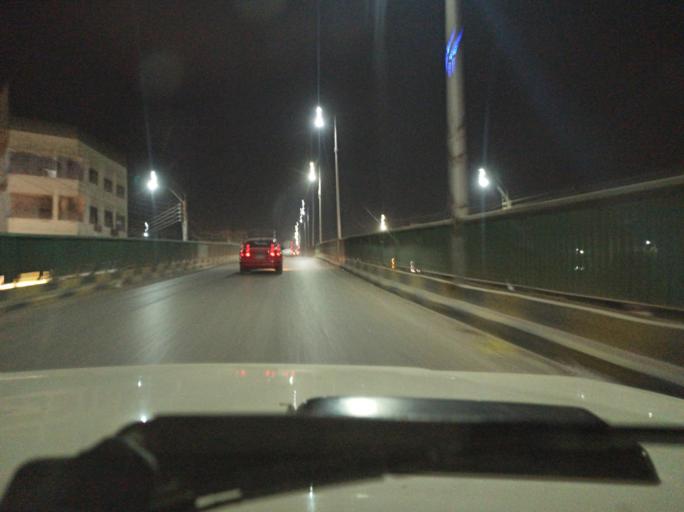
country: EG
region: Muhafazat Bani Suwayf
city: Bani Suwayf
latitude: 29.0761
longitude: 31.0909
